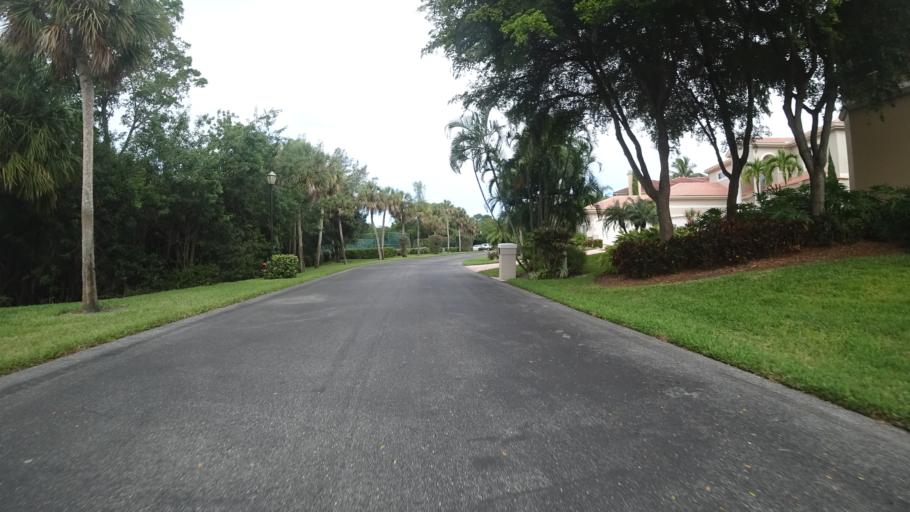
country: US
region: Florida
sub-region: Manatee County
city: Longboat Key
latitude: 27.4116
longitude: -82.6557
